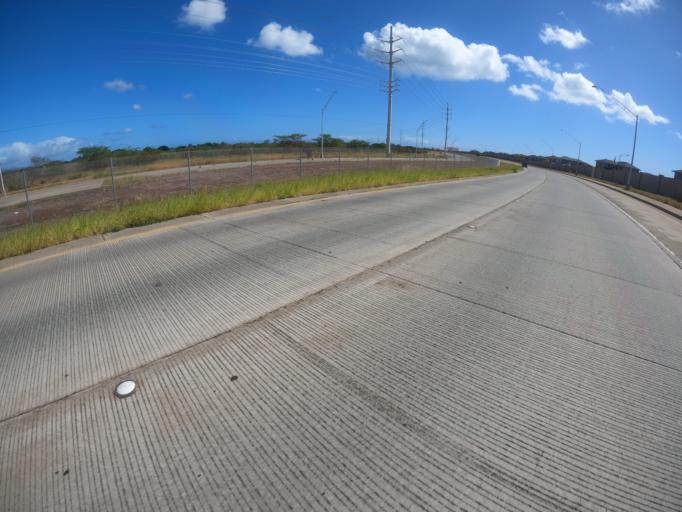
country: US
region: Hawaii
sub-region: Honolulu County
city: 'Ewa Villages
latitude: 21.3427
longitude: -158.0537
